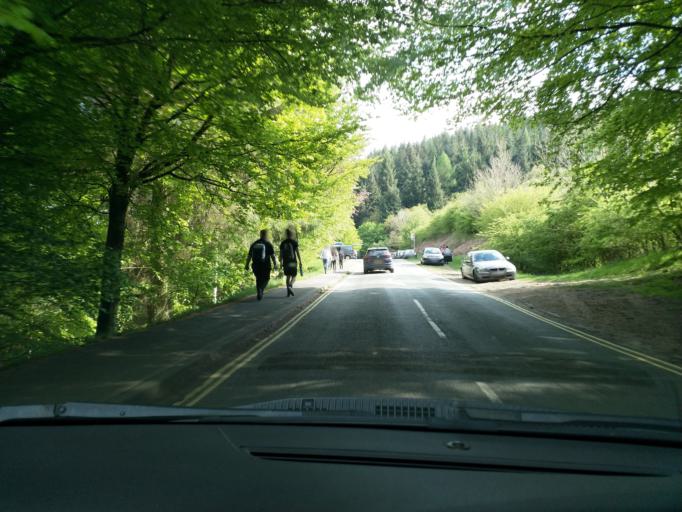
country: GB
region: England
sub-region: Derbyshire
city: Hope Valley
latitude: 53.3859
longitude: -1.7203
